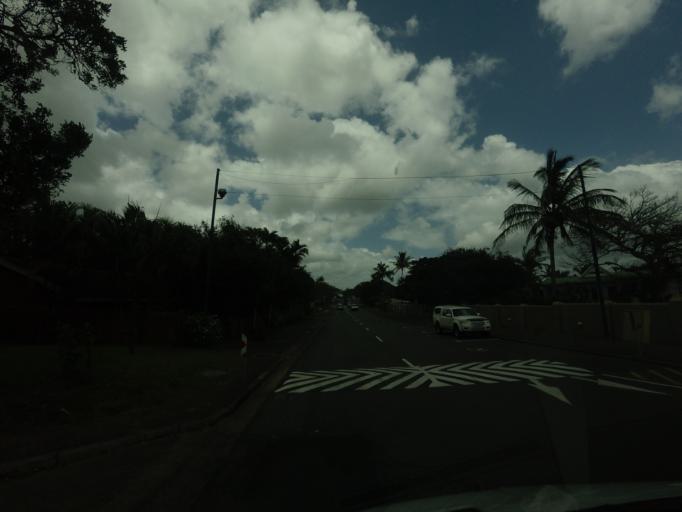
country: ZA
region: KwaZulu-Natal
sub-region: uMkhanyakude District Municipality
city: Mtubatuba
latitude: -28.3724
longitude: 32.4128
